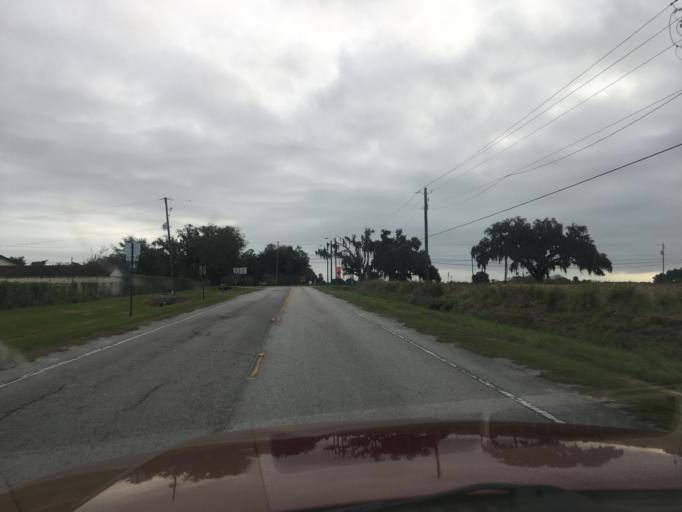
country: US
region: Florida
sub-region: Hillsborough County
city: Plant City
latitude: 28.0476
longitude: -82.0985
